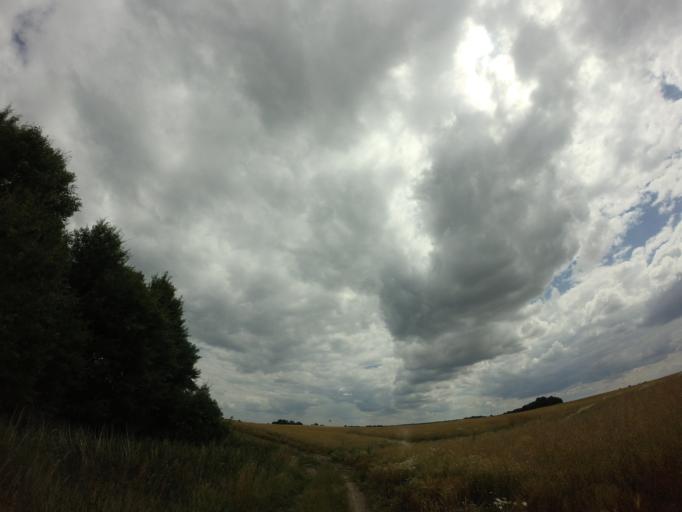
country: PL
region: West Pomeranian Voivodeship
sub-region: Powiat choszczenski
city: Recz
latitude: 53.1819
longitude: 15.5685
